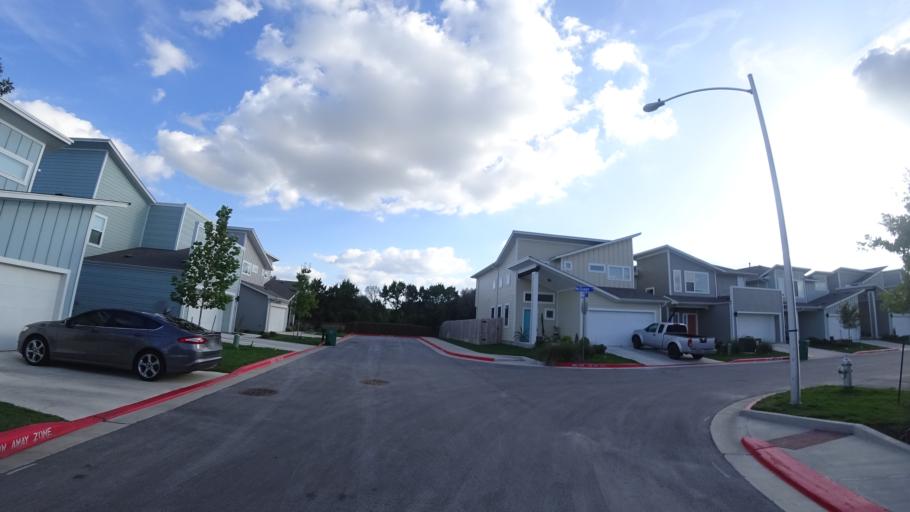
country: US
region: Texas
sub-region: Travis County
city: Onion Creek
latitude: 30.1896
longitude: -97.7924
